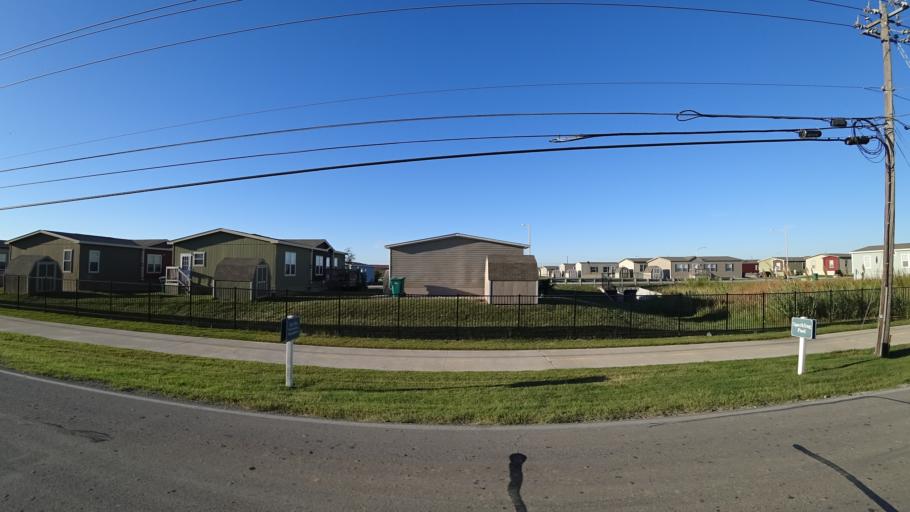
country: US
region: Texas
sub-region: Travis County
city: Manor
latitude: 30.3141
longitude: -97.6197
